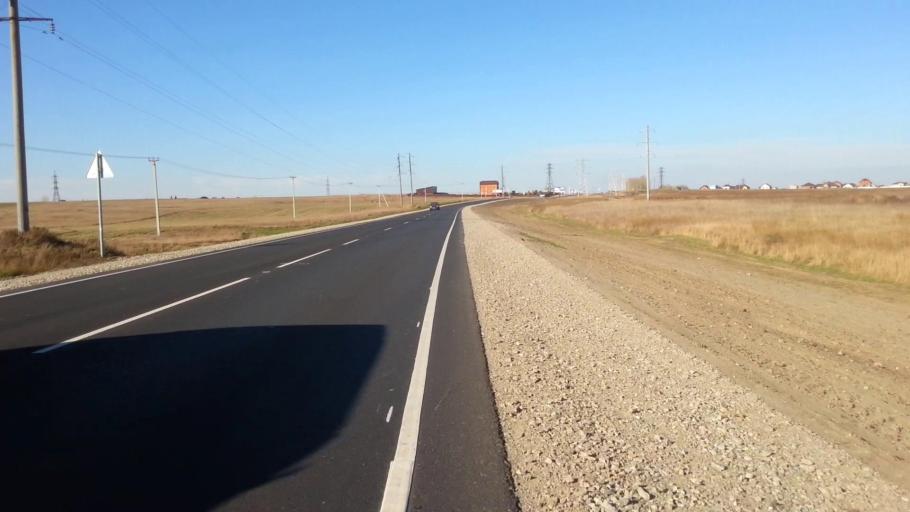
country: RU
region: Altai Krai
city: Sannikovo
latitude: 53.3306
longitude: 83.9383
